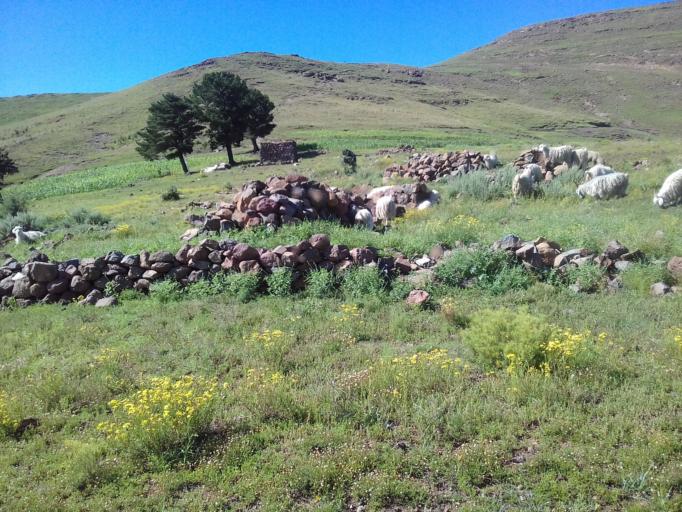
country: LS
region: Thaba-Tseka
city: Thaba-Tseka
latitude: -29.5249
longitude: 28.5802
